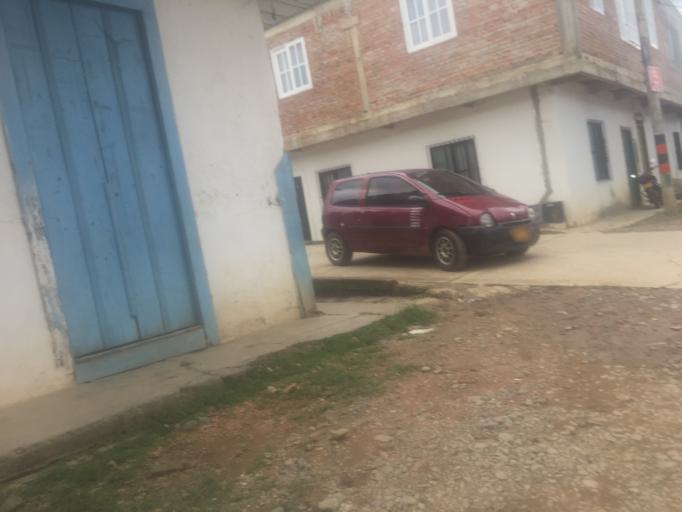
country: CO
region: Valle del Cauca
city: Calimita
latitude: 3.9336
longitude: -76.4853
